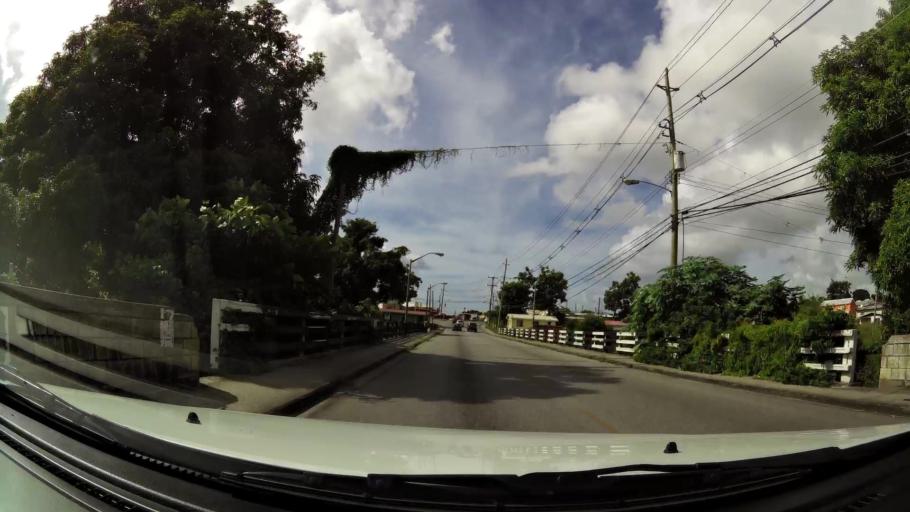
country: BB
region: Saint Michael
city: Bridgetown
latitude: 13.1069
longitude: -59.6046
